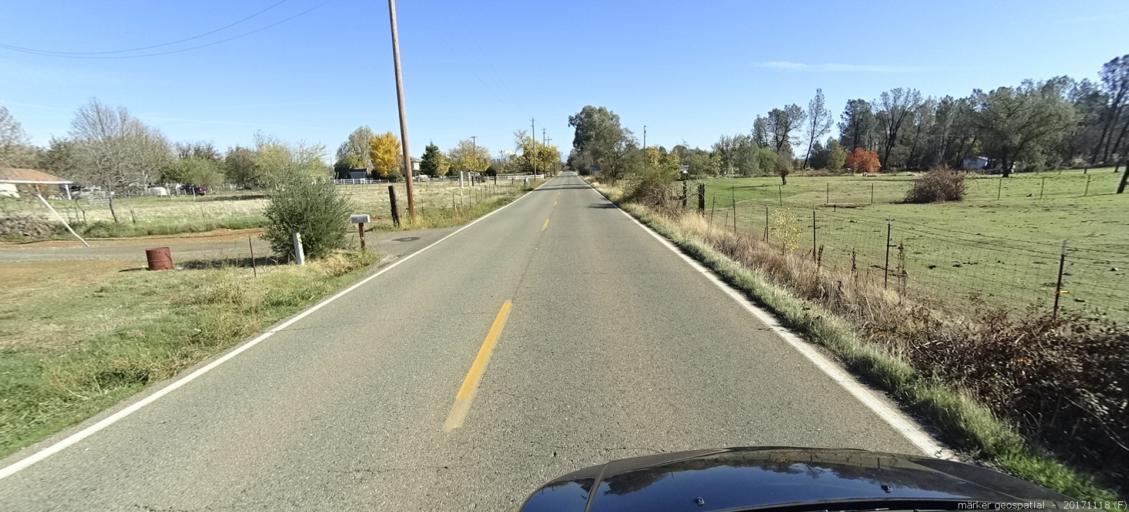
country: US
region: California
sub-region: Shasta County
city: Anderson
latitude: 40.4391
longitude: -122.3957
